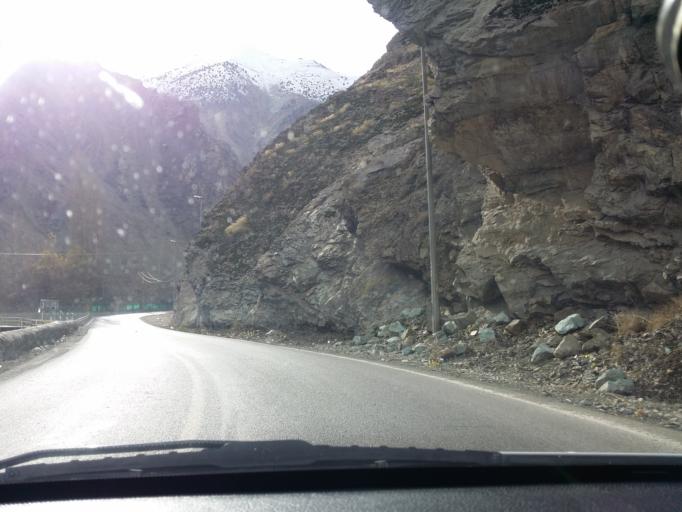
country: IR
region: Alborz
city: Karaj
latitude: 36.0367
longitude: 51.1789
